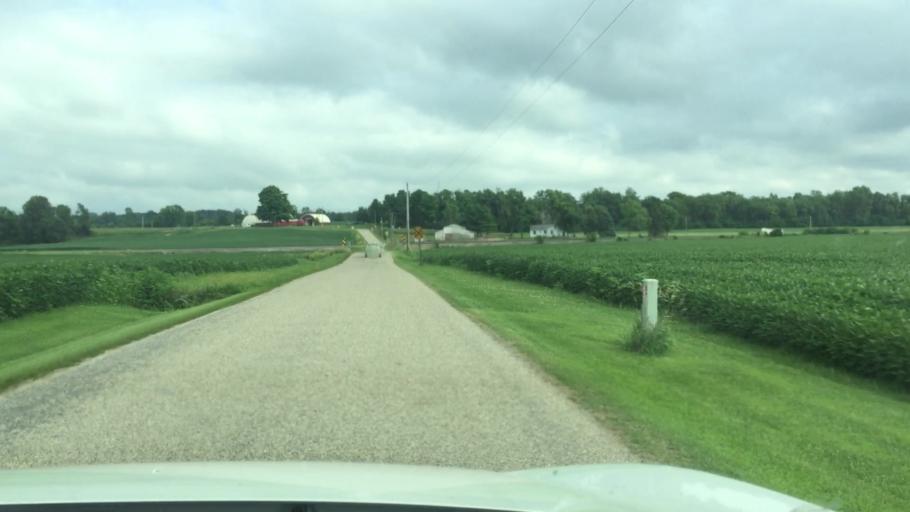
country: US
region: Ohio
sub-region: Champaign County
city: Mechanicsburg
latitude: 40.0493
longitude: -83.6349
